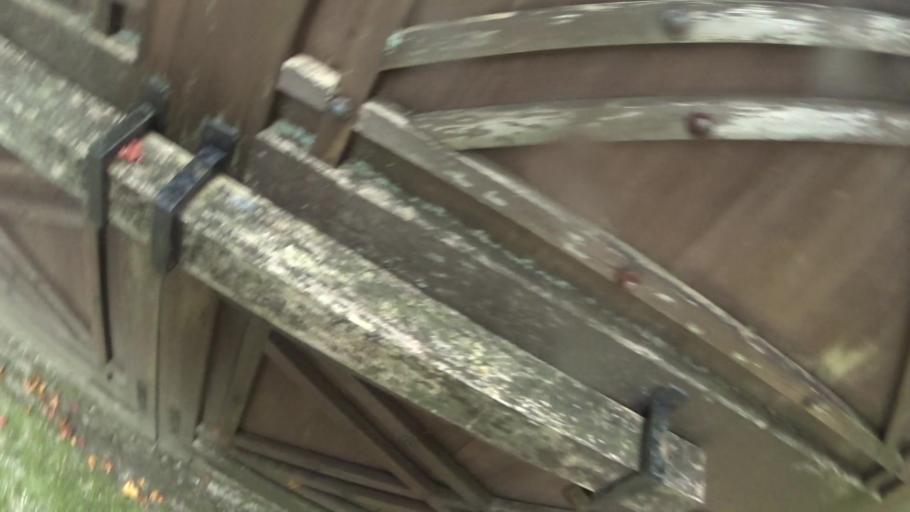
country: JP
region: Kyoto
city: Kyoto
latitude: 34.9776
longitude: 135.7814
